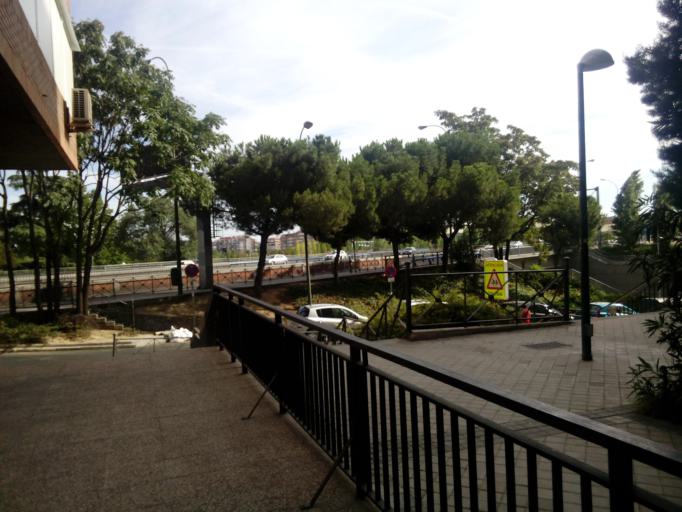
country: ES
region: Madrid
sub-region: Provincia de Madrid
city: Arganzuela
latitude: 40.3974
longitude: -3.7033
